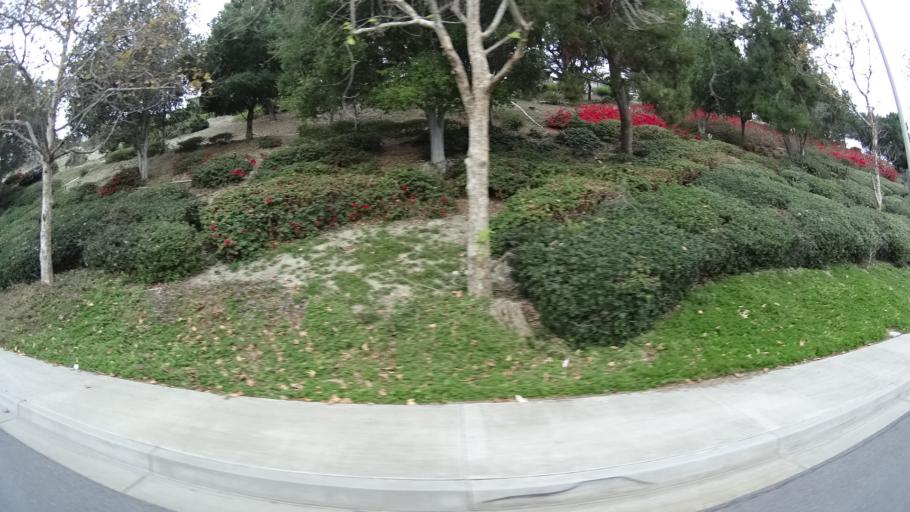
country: US
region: California
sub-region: Orange County
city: Aliso Viejo
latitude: 33.5706
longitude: -117.7357
